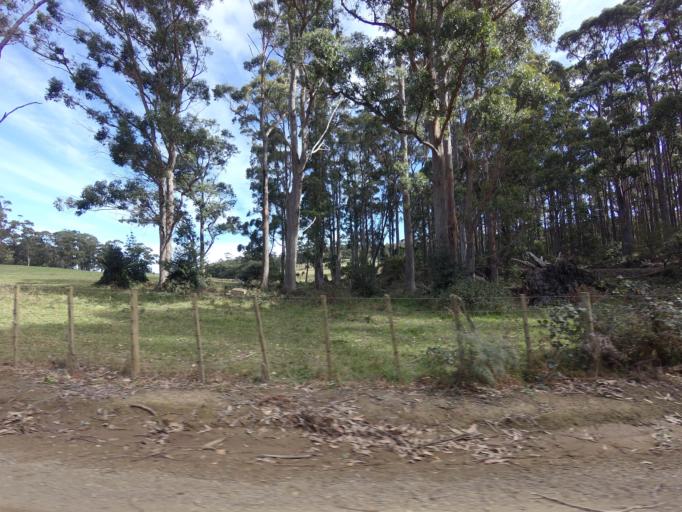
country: AU
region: Tasmania
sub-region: Clarence
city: Sandford
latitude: -43.1532
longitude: 147.7631
